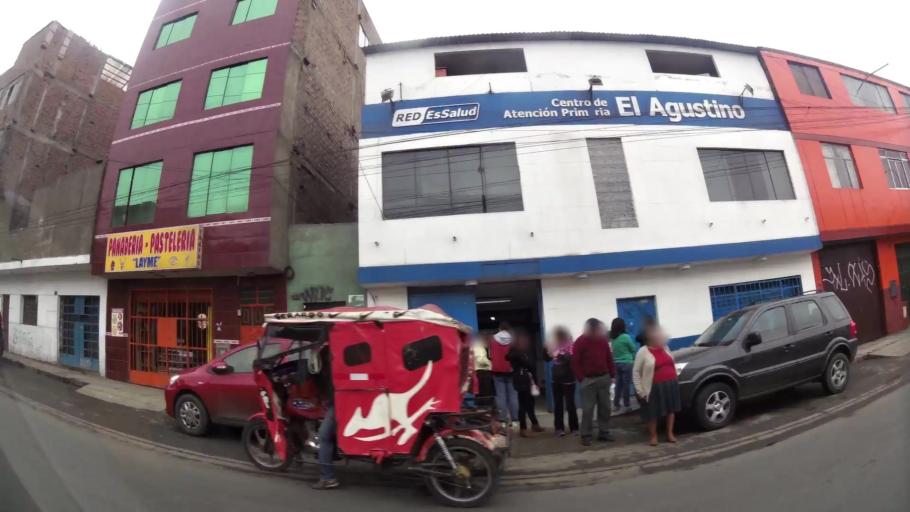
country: PE
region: Lima
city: Lima
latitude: -12.0446
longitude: -76.9981
